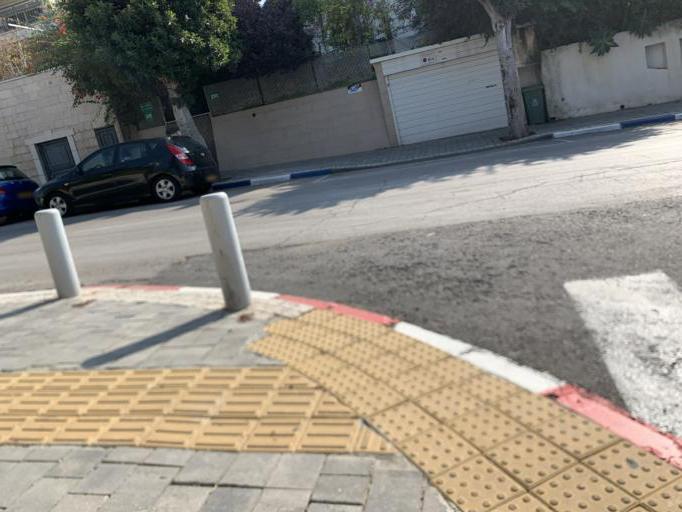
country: IL
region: Tel Aviv
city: Ramat Gan
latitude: 32.0923
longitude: 34.8130
